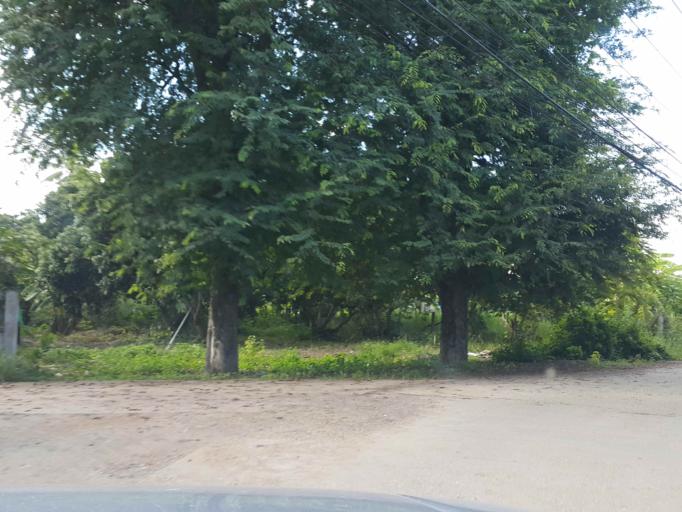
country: TH
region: Chiang Mai
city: Mae Taeng
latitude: 18.9701
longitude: 98.9158
